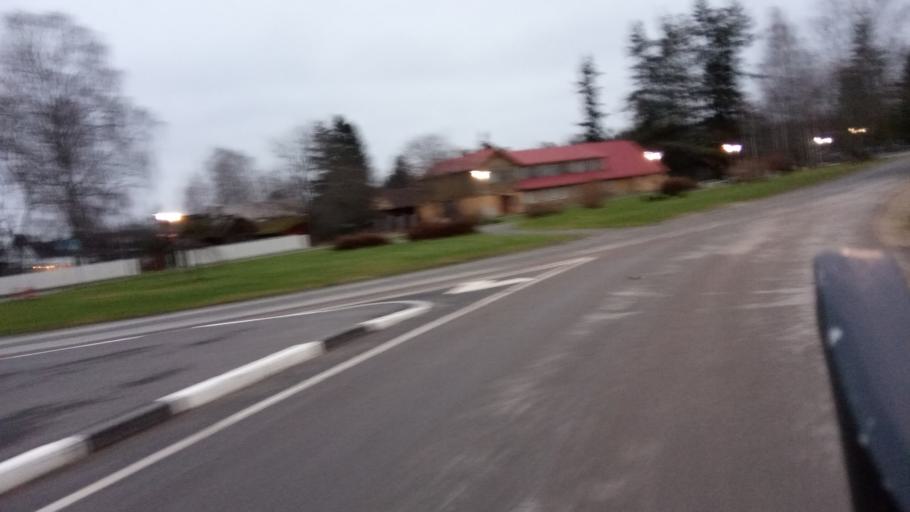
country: EE
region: Harju
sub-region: Kuusalu vald
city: Kuusalu
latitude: 59.4455
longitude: 25.4472
